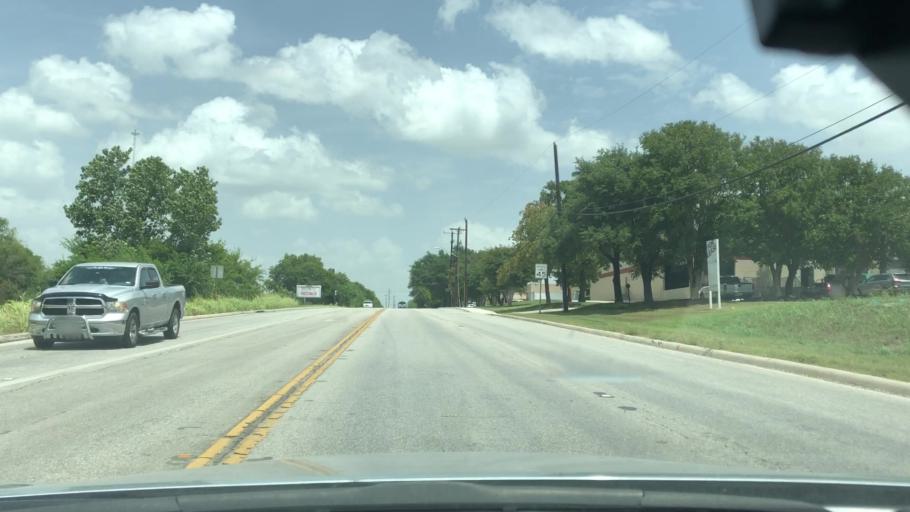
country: US
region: Texas
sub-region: Bexar County
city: Kirby
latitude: 29.4556
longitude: -98.4103
